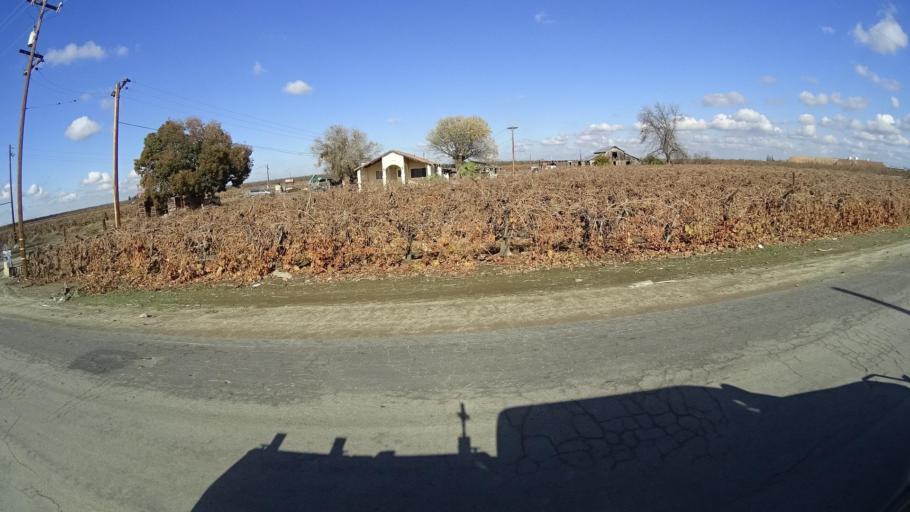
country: US
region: California
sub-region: Kern County
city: McFarland
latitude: 35.6888
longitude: -119.2508
